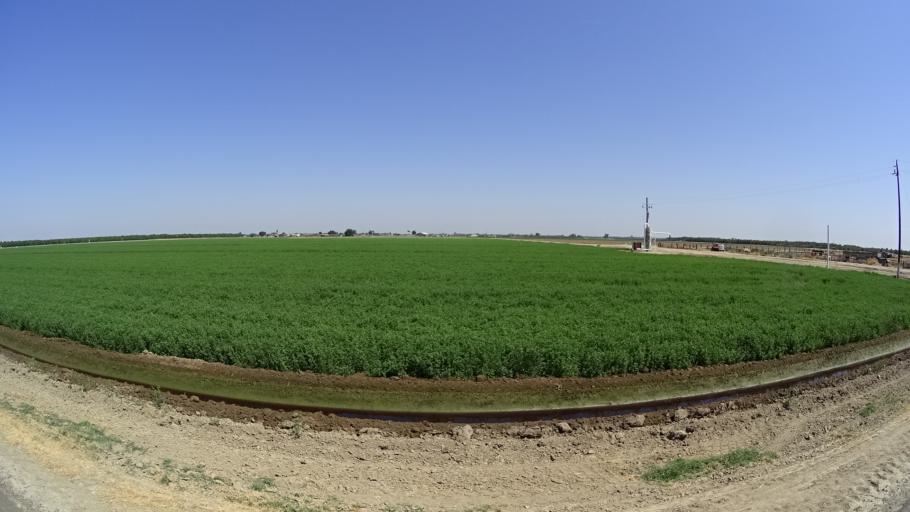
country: US
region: California
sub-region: Kings County
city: Armona
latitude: 36.3716
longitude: -119.7229
